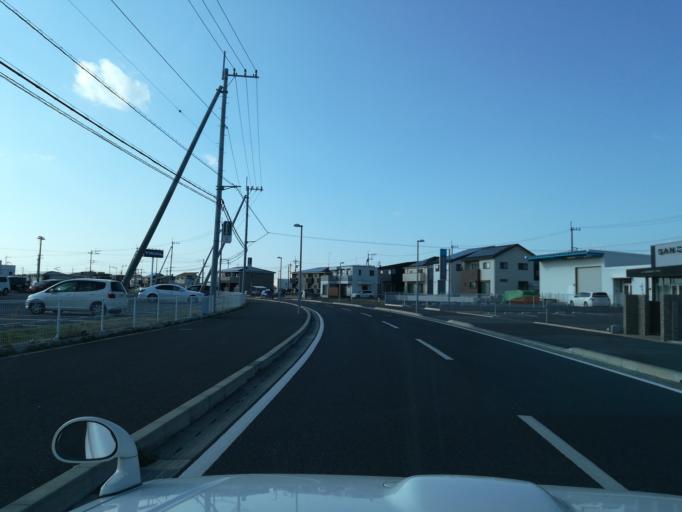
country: JP
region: Ibaraki
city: Naka
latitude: 36.0962
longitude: 140.0879
